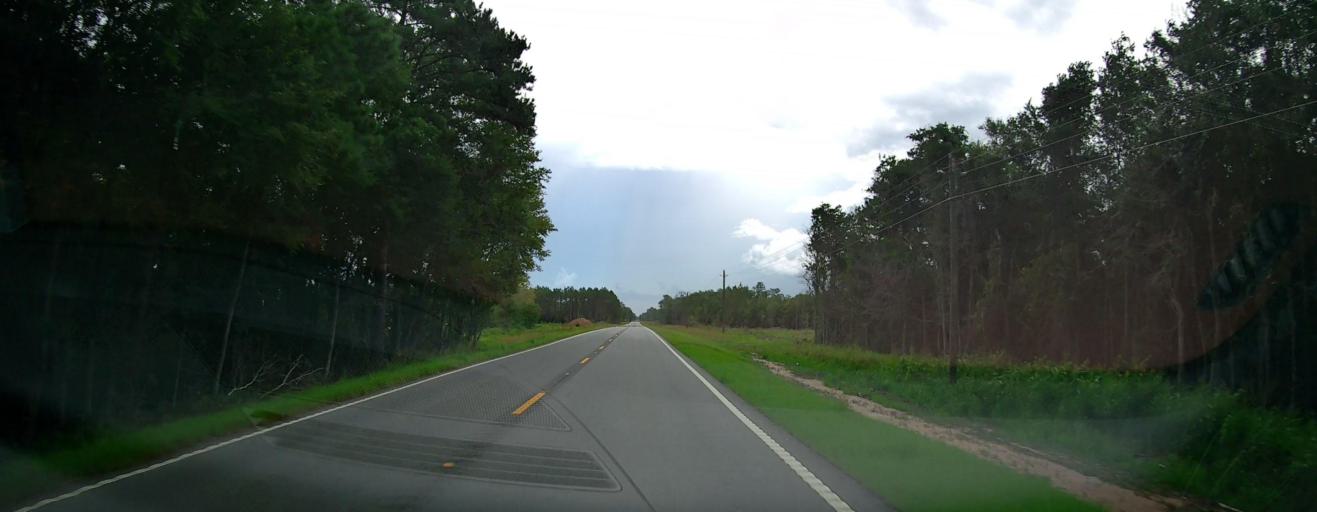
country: US
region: Georgia
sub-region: Pierce County
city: Blackshear
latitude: 31.3687
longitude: -82.0960
